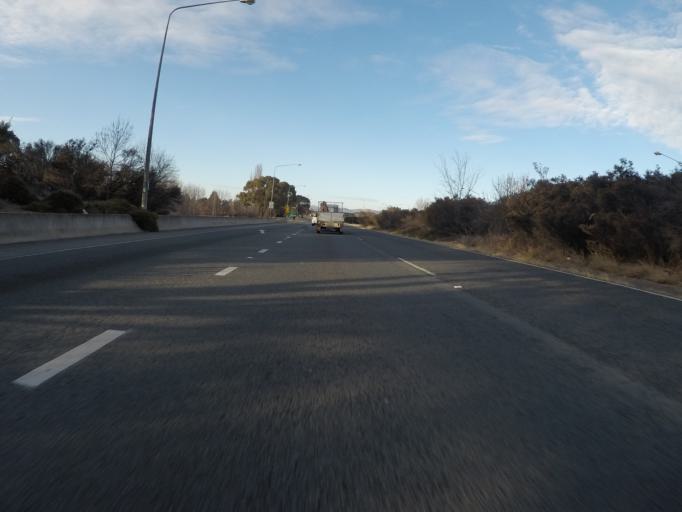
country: AU
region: Australian Capital Territory
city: Forrest
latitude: -35.3360
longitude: 149.1623
